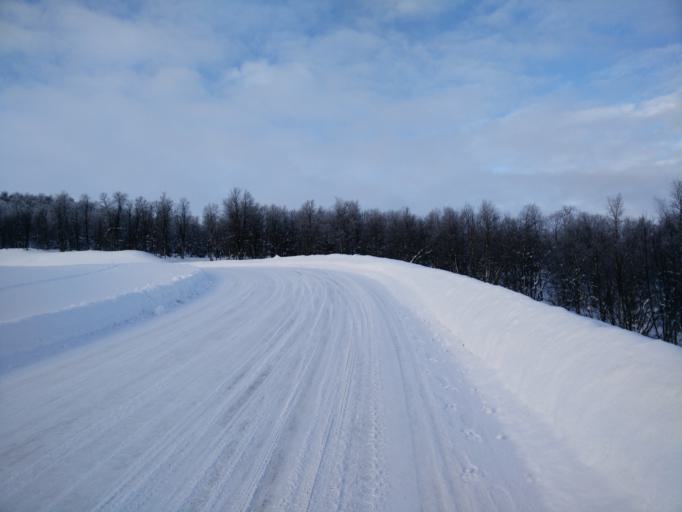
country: NO
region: Sor-Trondelag
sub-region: Tydal
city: Aas
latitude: 62.6517
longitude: 12.4097
